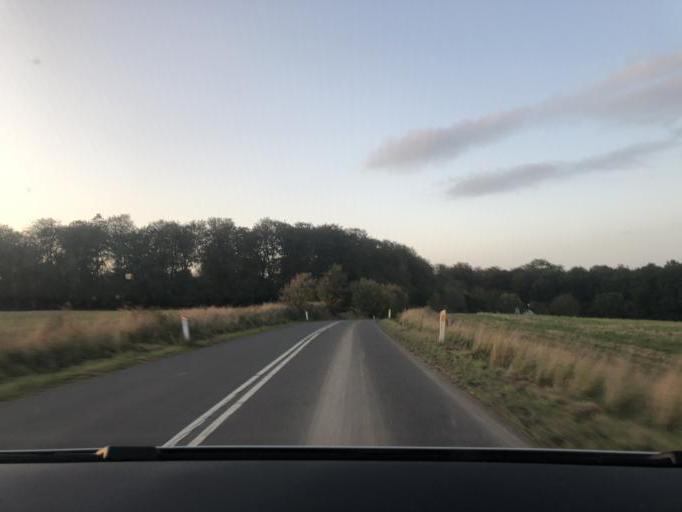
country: DK
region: Capital Region
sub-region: Egedal Kommune
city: Stenlose
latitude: 55.8073
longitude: 12.2107
